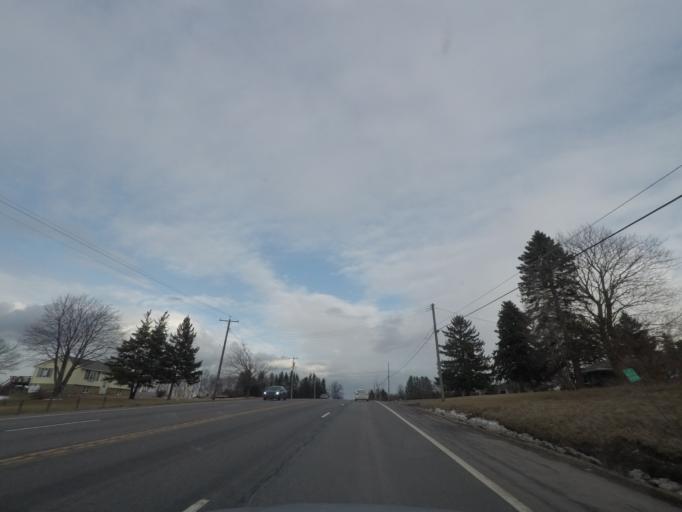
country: US
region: New York
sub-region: Oneida County
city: Clark Mills
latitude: 43.0802
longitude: -75.4183
